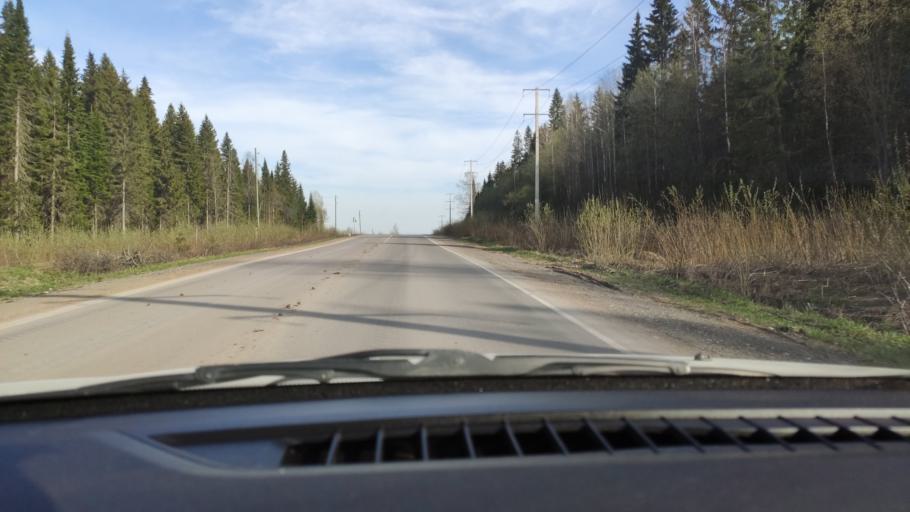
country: RU
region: Perm
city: Novyye Lyady
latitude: 57.9201
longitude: 56.6629
